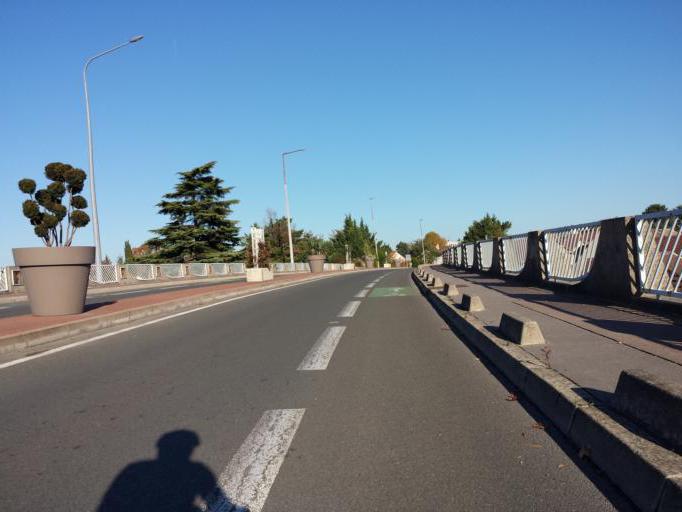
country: FR
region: Ile-de-France
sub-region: Departement du Val-d'Oise
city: Ermont
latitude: 48.9926
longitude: 2.2629
